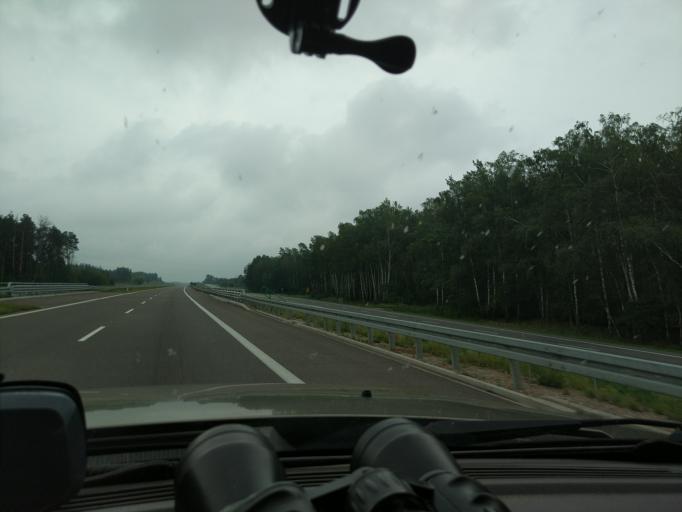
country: PL
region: Podlasie
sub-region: Powiat zambrowski
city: Rutki-Kossaki
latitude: 53.0658
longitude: 22.4130
